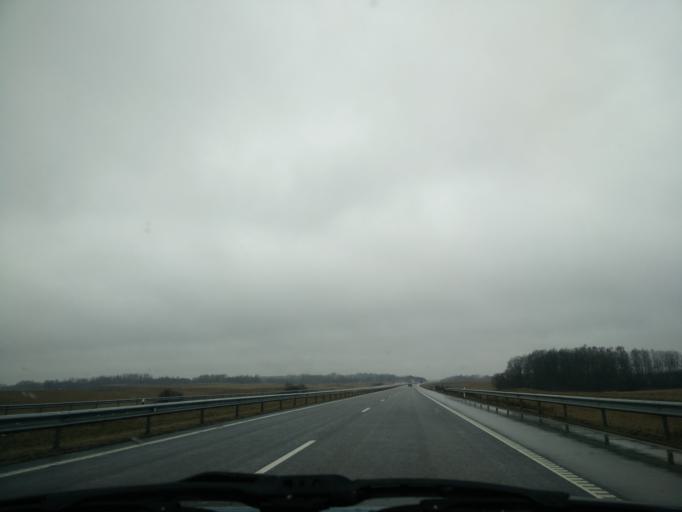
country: LT
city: Skaudvile
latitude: 55.4850
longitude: 22.5779
